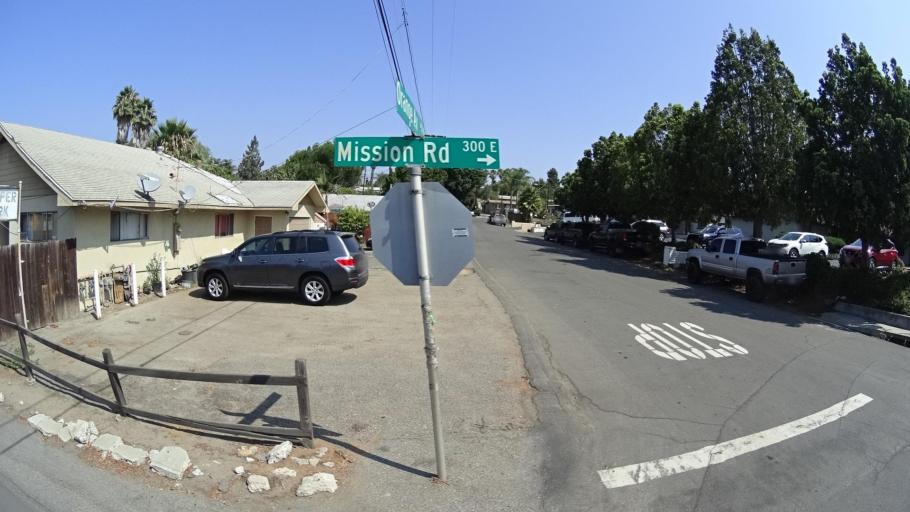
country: US
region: California
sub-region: San Diego County
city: Fallbrook
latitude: 33.3847
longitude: -117.2491
